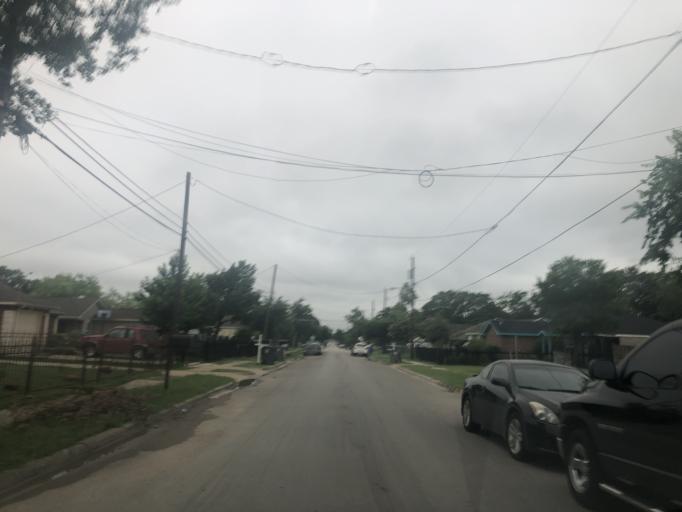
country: US
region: Texas
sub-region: Dallas County
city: Cockrell Hill
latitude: 32.7807
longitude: -96.8757
